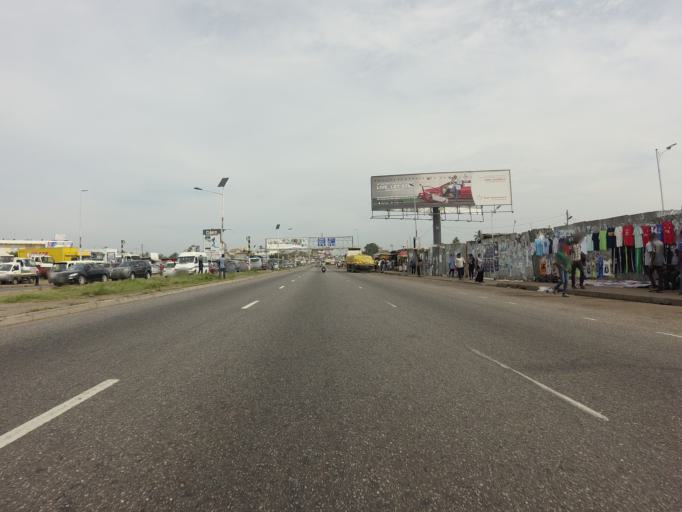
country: GH
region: Greater Accra
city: Dome
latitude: 5.6139
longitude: -0.2288
